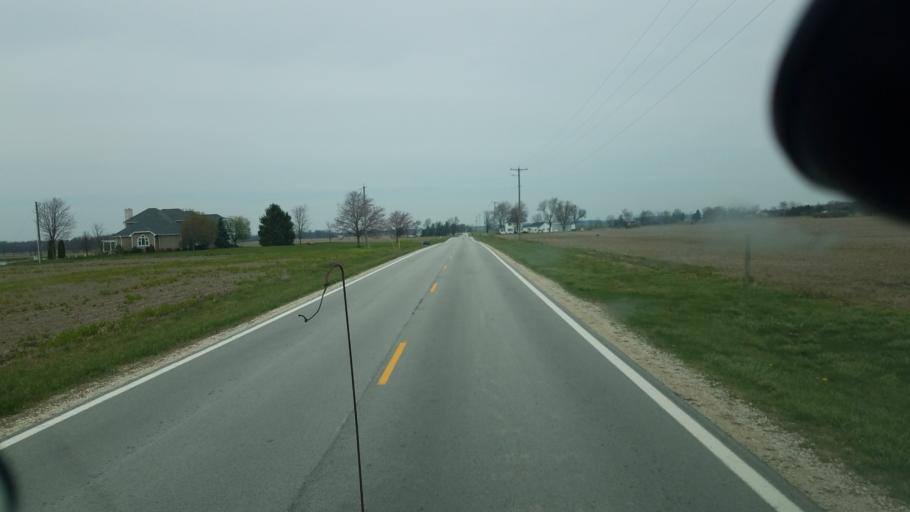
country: US
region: Ohio
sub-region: Wyandot County
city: Carey
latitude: 40.9780
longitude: -83.4767
